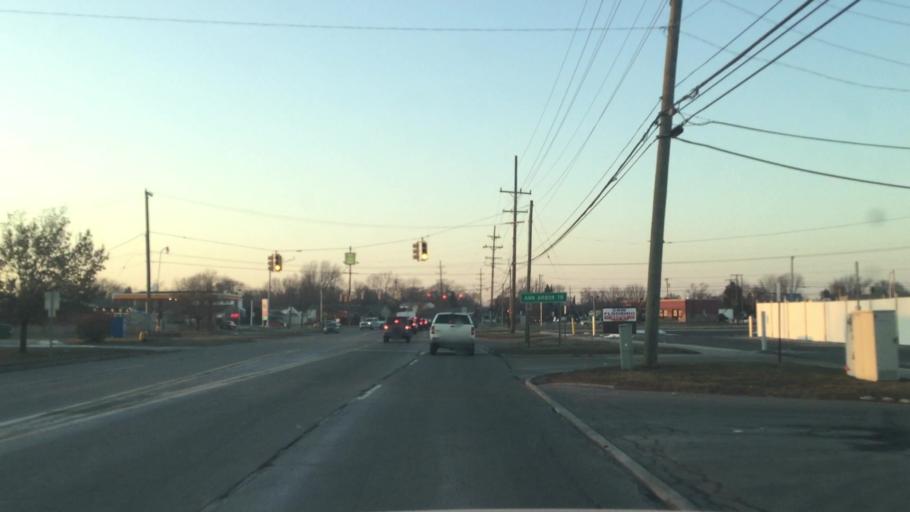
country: US
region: Michigan
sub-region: Wayne County
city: Livonia
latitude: 42.3454
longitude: -83.3505
